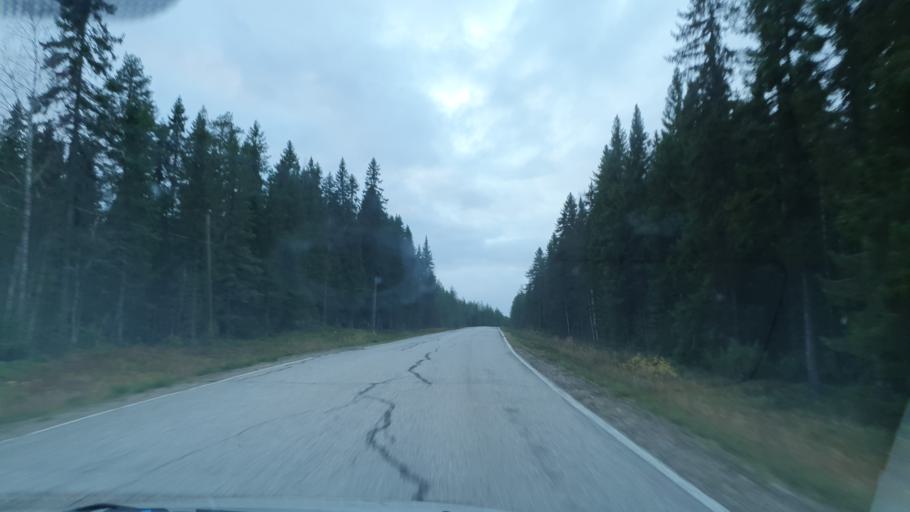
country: FI
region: Kainuu
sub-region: Kajaani
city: Ristijaervi
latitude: 64.4286
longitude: 28.3767
